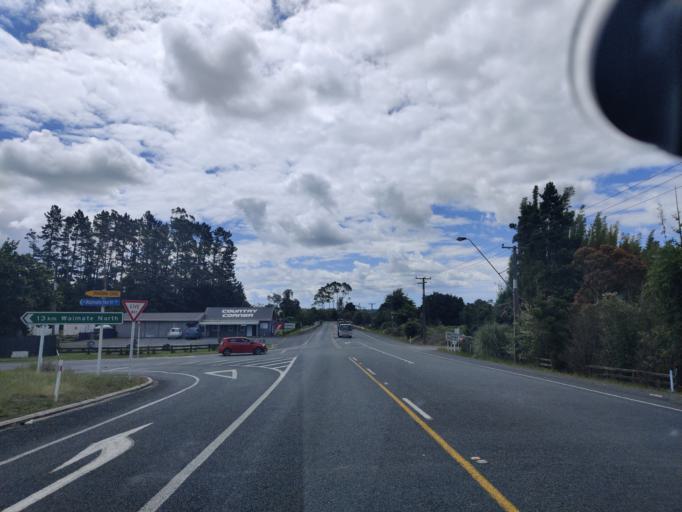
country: NZ
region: Northland
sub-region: Far North District
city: Kerikeri
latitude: -35.2360
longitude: 173.9173
